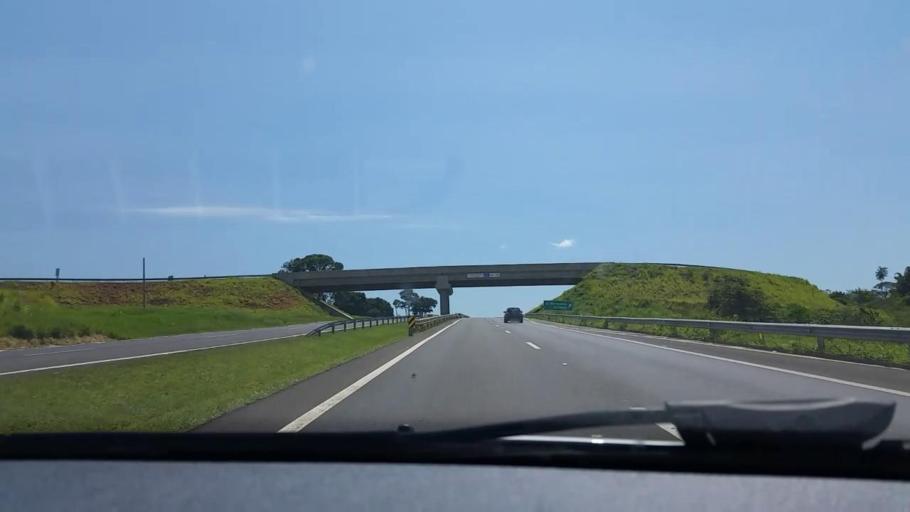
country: BR
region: Sao Paulo
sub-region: Bauru
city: Bauru
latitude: -22.3995
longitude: -49.0890
